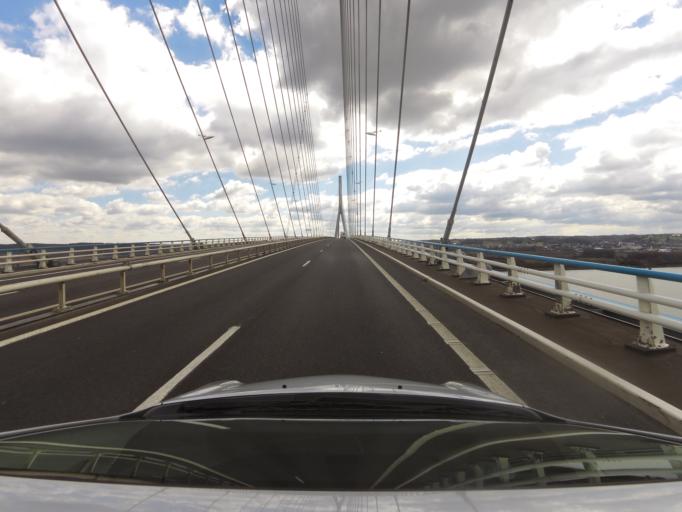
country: FR
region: Lower Normandy
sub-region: Departement du Calvados
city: La Riviere-Saint-Sauveur
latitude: 49.4349
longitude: 0.2735
